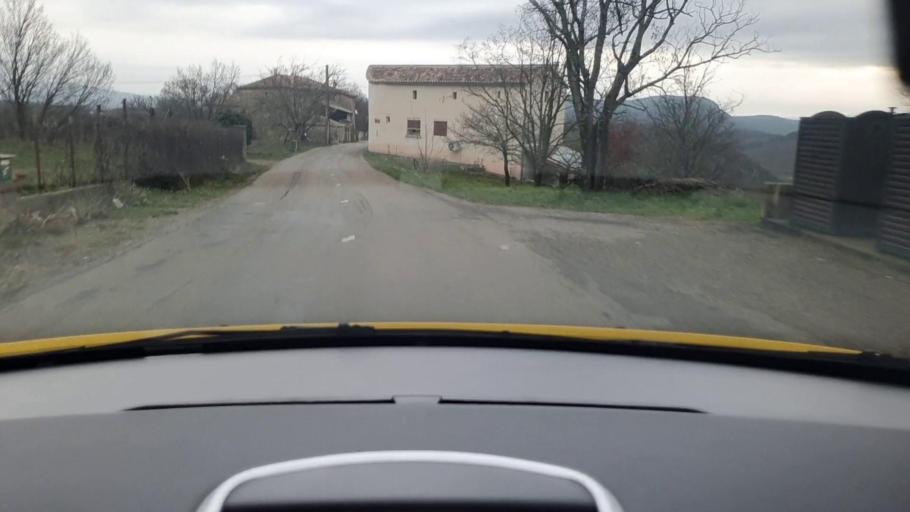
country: FR
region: Languedoc-Roussillon
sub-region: Departement du Gard
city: Molieres-sur-Ceze
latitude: 44.2989
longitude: 4.1594
